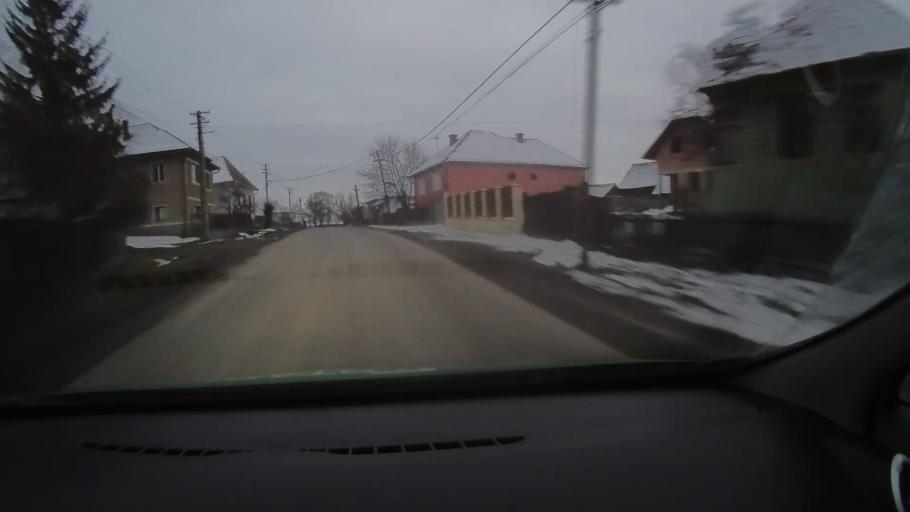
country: RO
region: Harghita
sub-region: Comuna Darjiu
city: Darjiu
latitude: 46.2119
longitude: 25.2399
